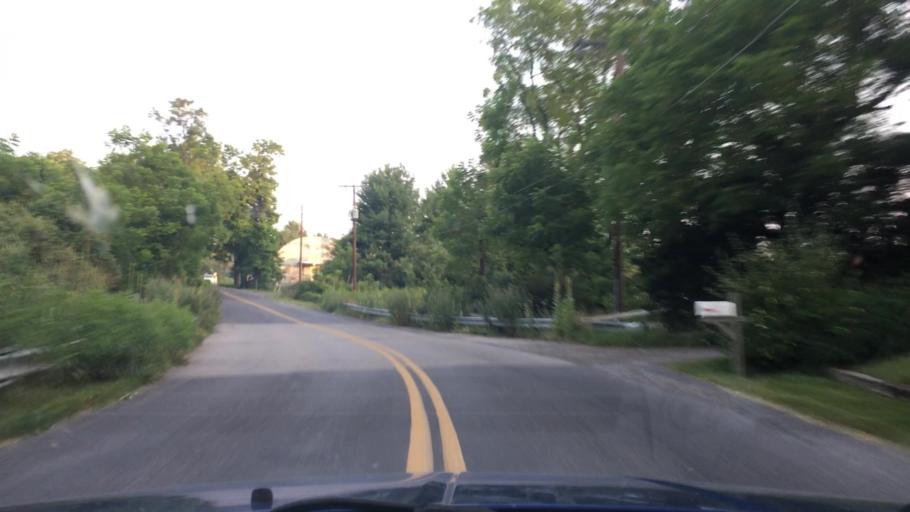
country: US
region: Virginia
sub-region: Augusta County
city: Verona
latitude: 38.2397
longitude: -78.9703
